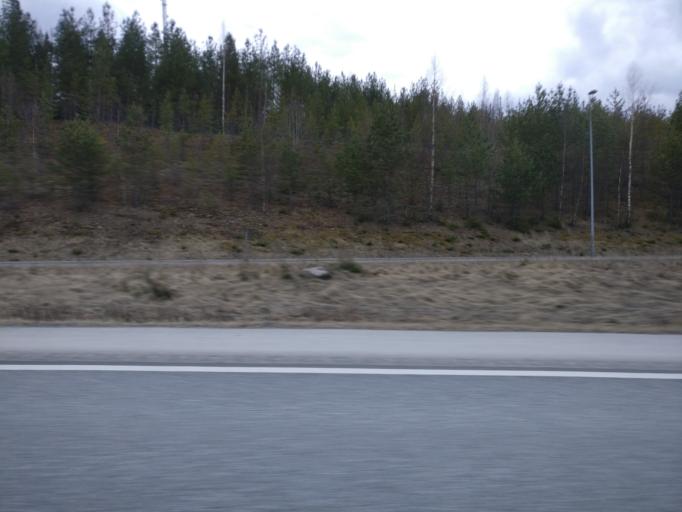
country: FI
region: Haeme
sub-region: Haemeenlinna
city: Janakkala
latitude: 60.9101
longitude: 24.5457
